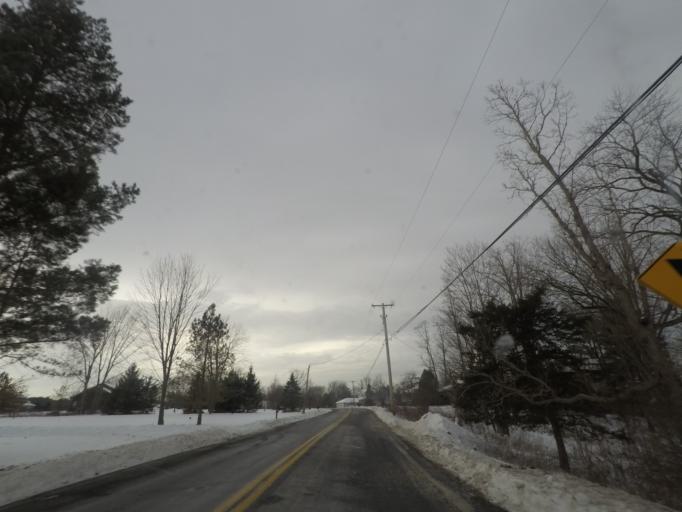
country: US
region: New York
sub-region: Rensselaer County
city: Castleton-on-Hudson
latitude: 42.5039
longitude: -73.7410
